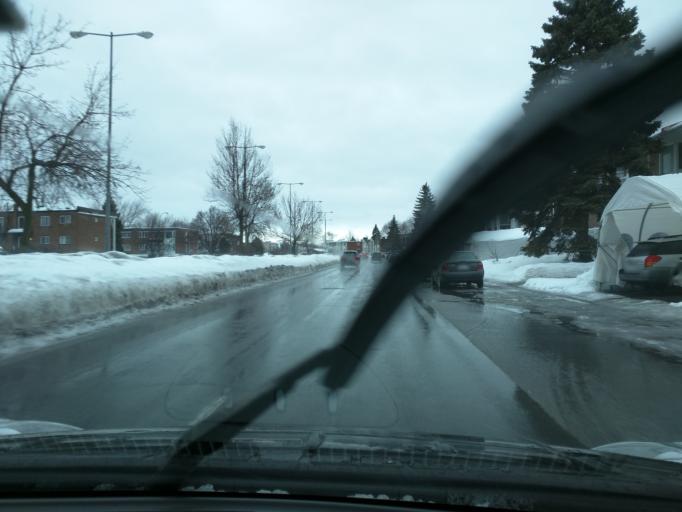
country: CA
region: Quebec
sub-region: Monteregie
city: Longueuil
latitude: 45.5172
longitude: -73.4647
